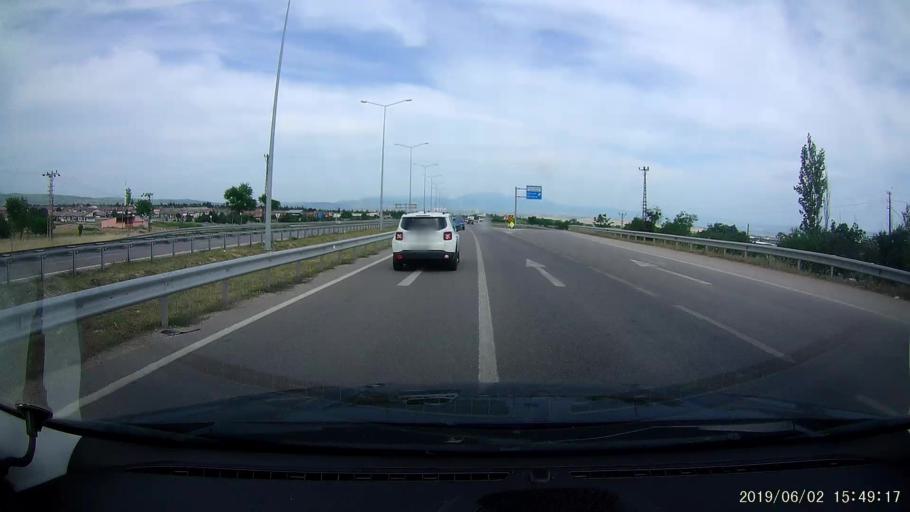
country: TR
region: Amasya
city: Merzifon
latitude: 40.8576
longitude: 35.4621
